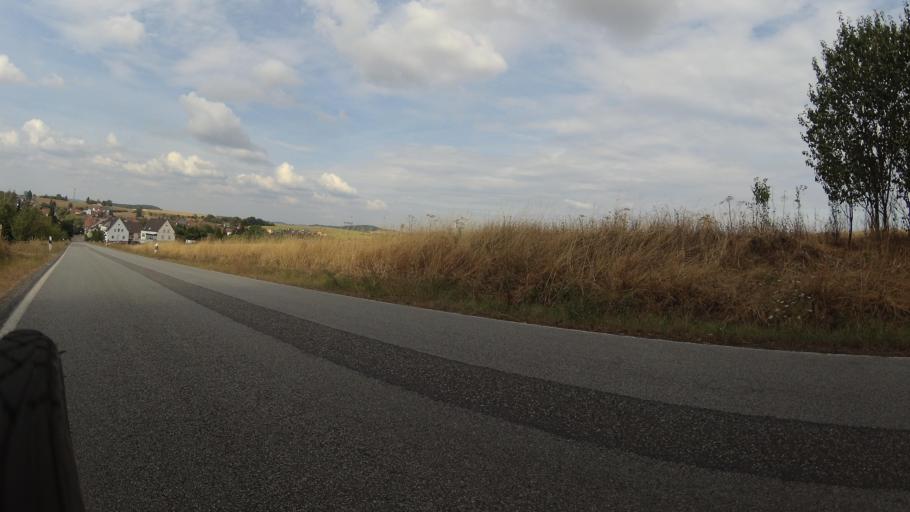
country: DE
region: Rheinland-Pfalz
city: Wahnwegen
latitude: 49.4794
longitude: 7.3766
